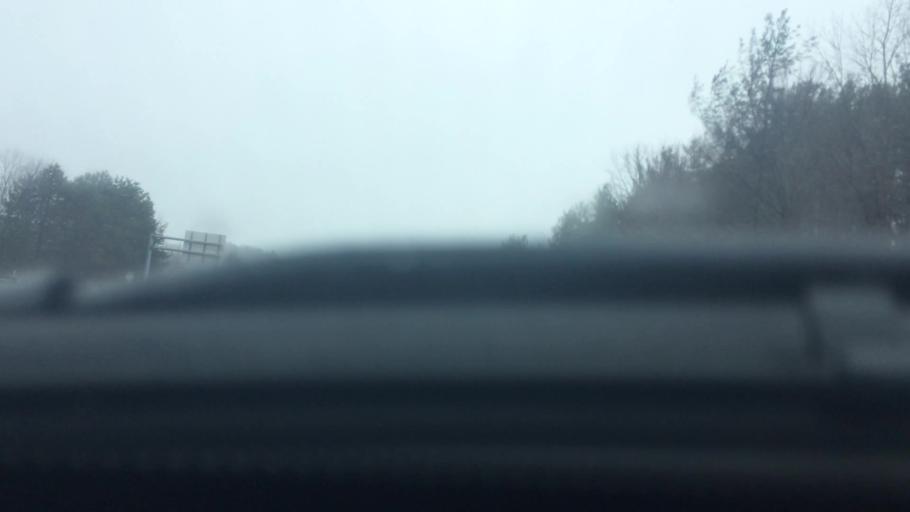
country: US
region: Massachusetts
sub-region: Essex County
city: Haverhill
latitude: 42.7530
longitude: -71.1119
